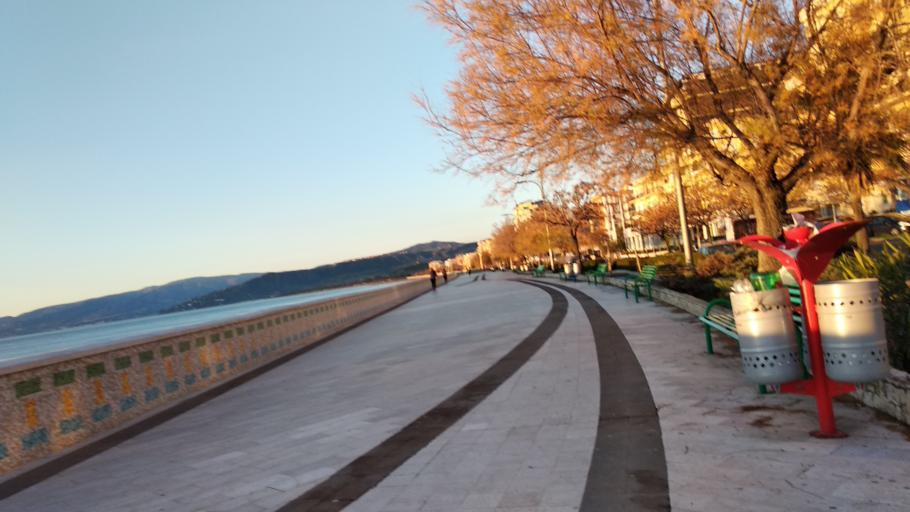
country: IT
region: Calabria
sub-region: Provincia di Catanzaro
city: Roccelletta
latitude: 38.8257
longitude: 16.6245
